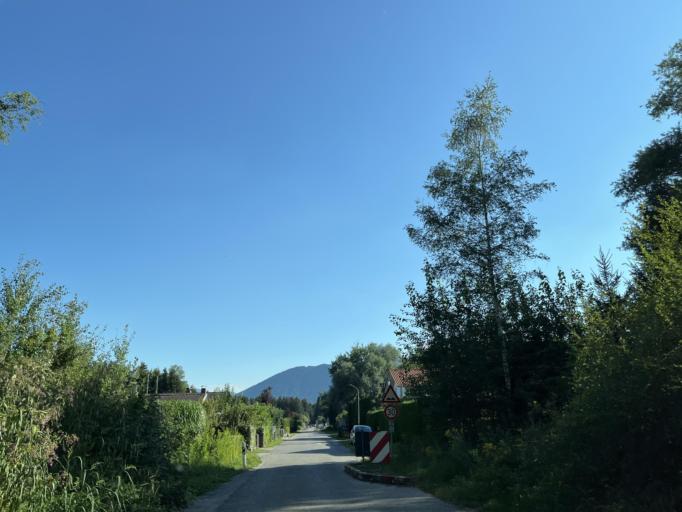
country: DE
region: Bavaria
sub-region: Upper Bavaria
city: Raubling
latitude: 47.8004
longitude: 12.0707
